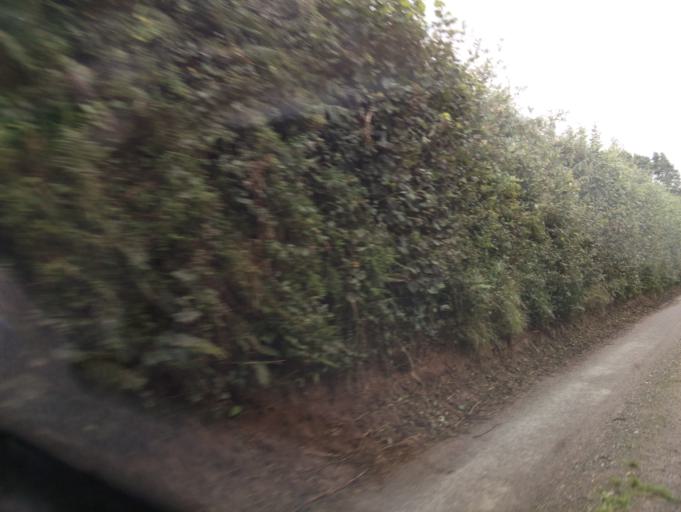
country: GB
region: England
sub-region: Devon
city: Kingsbridge
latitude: 50.2966
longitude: -3.7164
